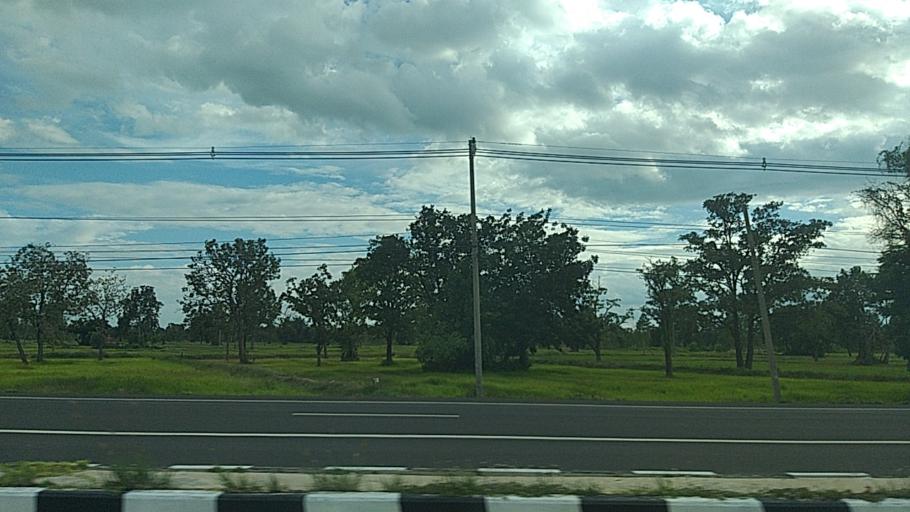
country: TH
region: Surin
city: Prasat
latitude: 14.5594
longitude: 103.5003
